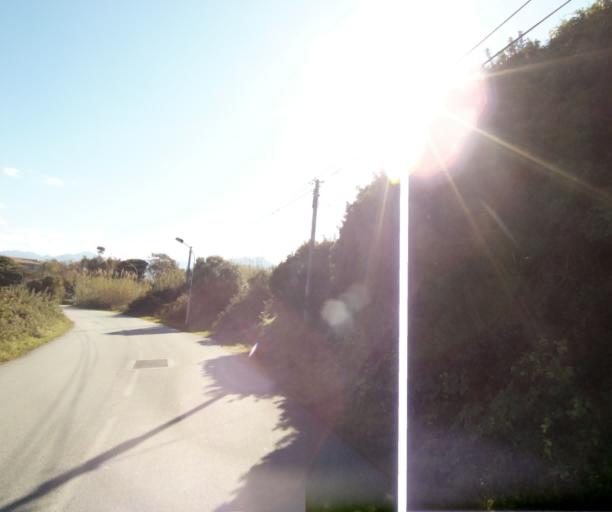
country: FR
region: Corsica
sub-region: Departement de la Corse-du-Sud
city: Propriano
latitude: 41.6727
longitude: 8.8958
